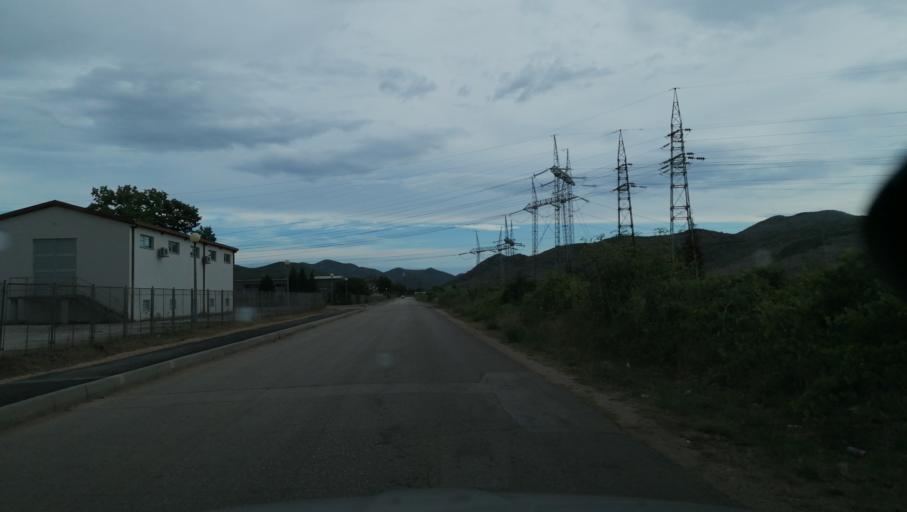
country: BA
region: Republika Srpska
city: Trebinje
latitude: 42.6782
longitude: 18.3322
